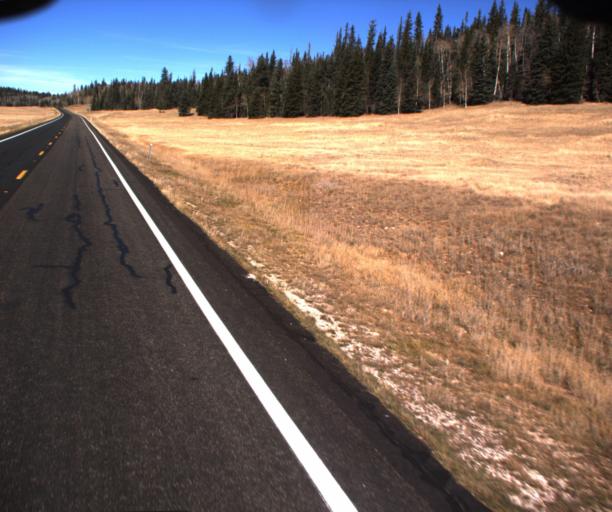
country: US
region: Arizona
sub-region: Coconino County
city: Grand Canyon
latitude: 36.4285
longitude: -112.1320
